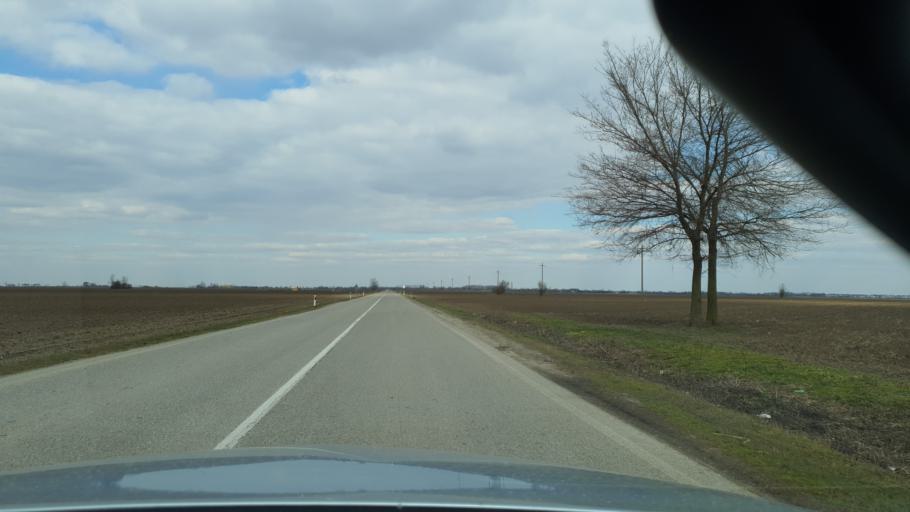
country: RS
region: Autonomna Pokrajina Vojvodina
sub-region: Juznobacki Okrug
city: Bac
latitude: 45.4273
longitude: 19.3069
